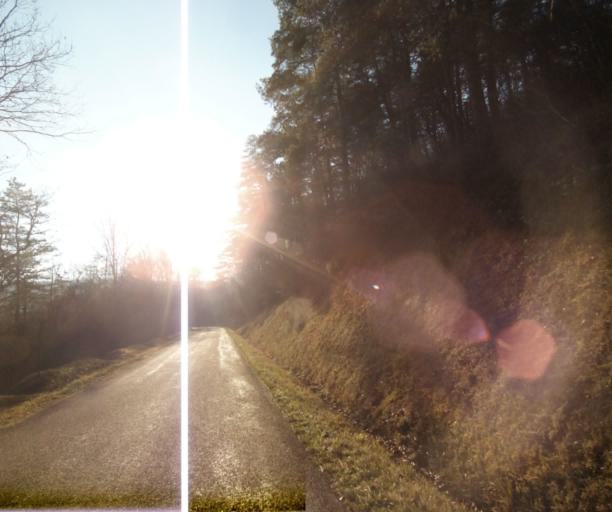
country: FR
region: Champagne-Ardenne
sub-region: Departement de la Haute-Marne
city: Chevillon
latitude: 48.5425
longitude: 5.1188
